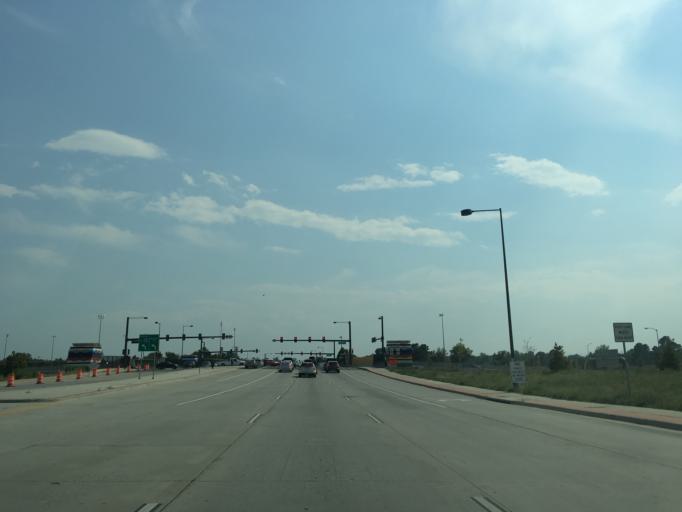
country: US
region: Colorado
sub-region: Denver County
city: Denver
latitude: 39.7271
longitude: -105.0252
